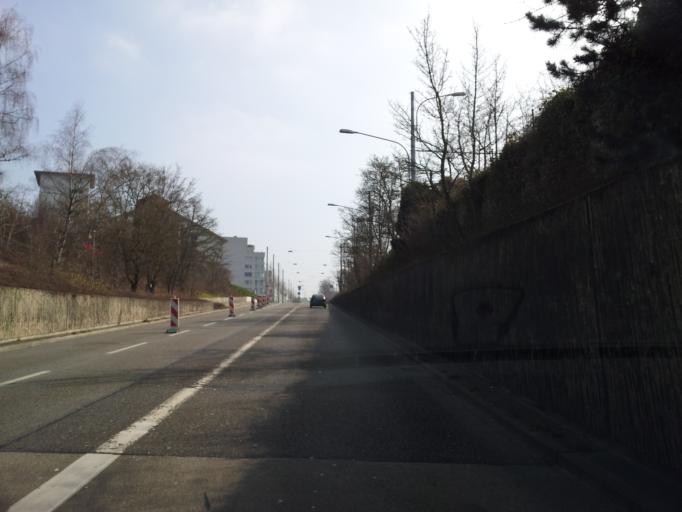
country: CH
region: Zurich
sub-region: Bezirk Zuerich
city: Zuerich (Kreis 11) / Affoltern
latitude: 47.4238
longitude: 8.4972
